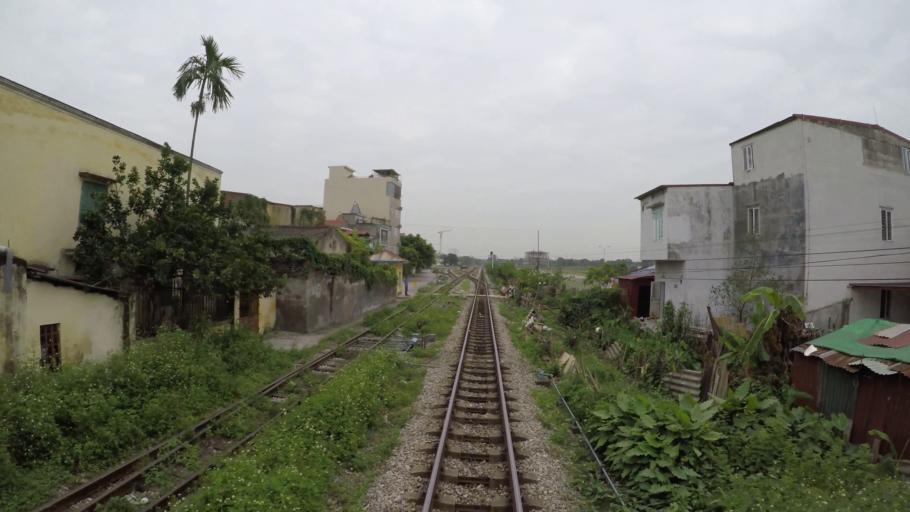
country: VN
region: Hai Phong
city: An Duong
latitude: 20.8842
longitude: 106.6046
